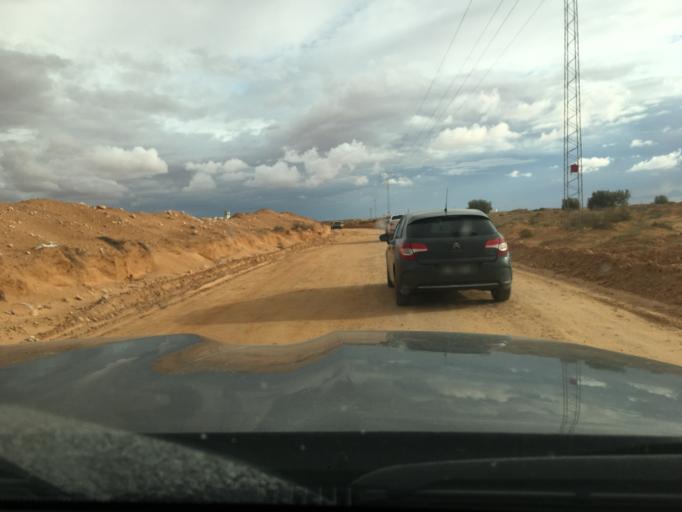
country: TN
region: Madanin
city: Medenine
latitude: 33.2715
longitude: 10.5668
